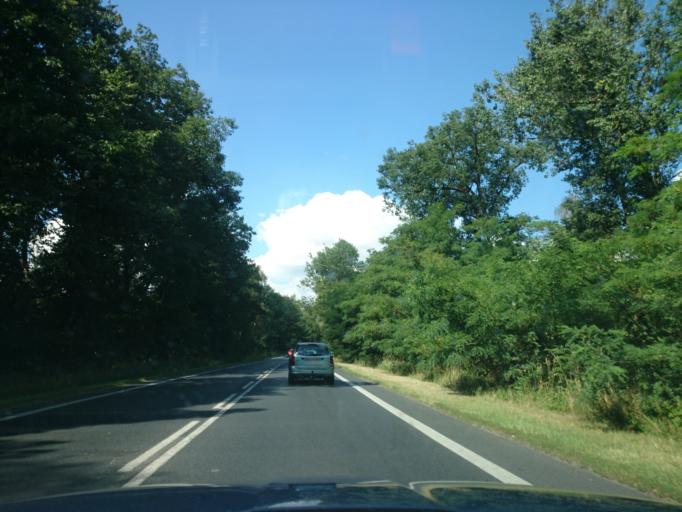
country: PL
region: West Pomeranian Voivodeship
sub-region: Szczecin
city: Szczecin
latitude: 53.3764
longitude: 14.5535
